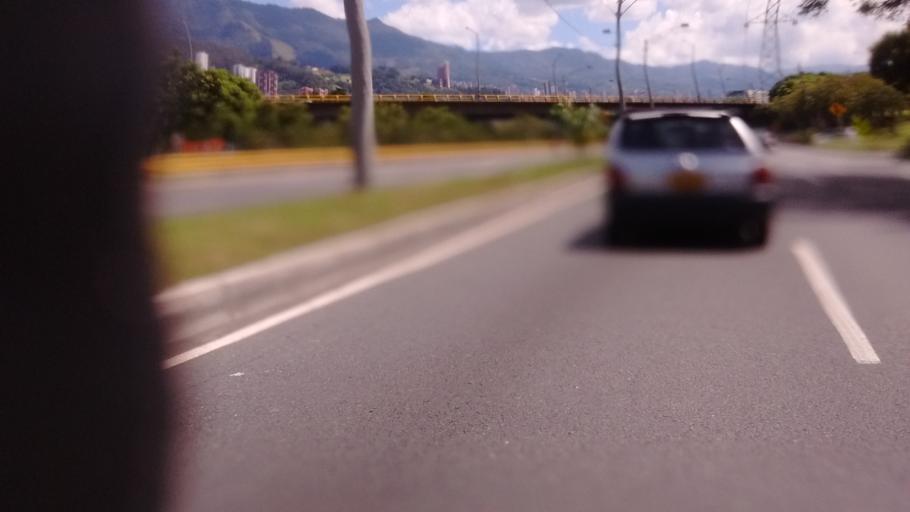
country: CO
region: Antioquia
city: Medellin
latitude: 6.2379
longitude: -75.5773
